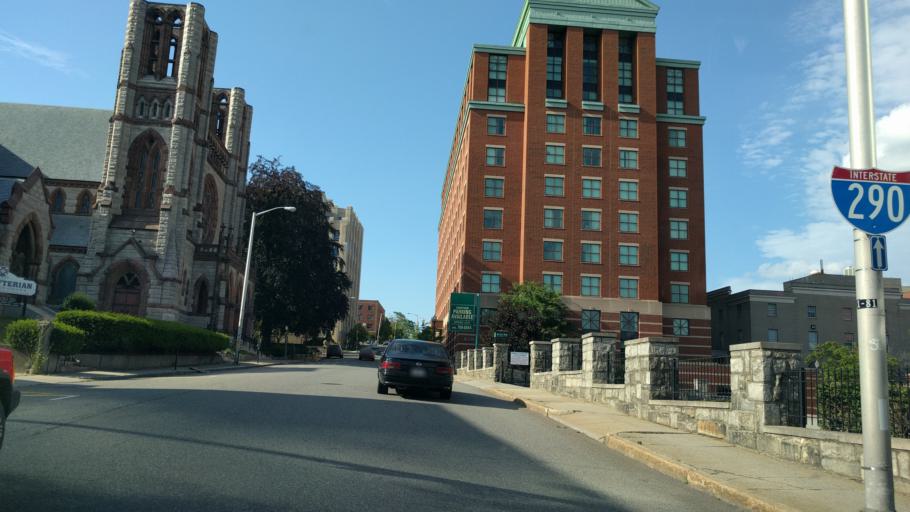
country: US
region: Massachusetts
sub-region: Worcester County
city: Worcester
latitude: 42.2637
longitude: -71.8044
